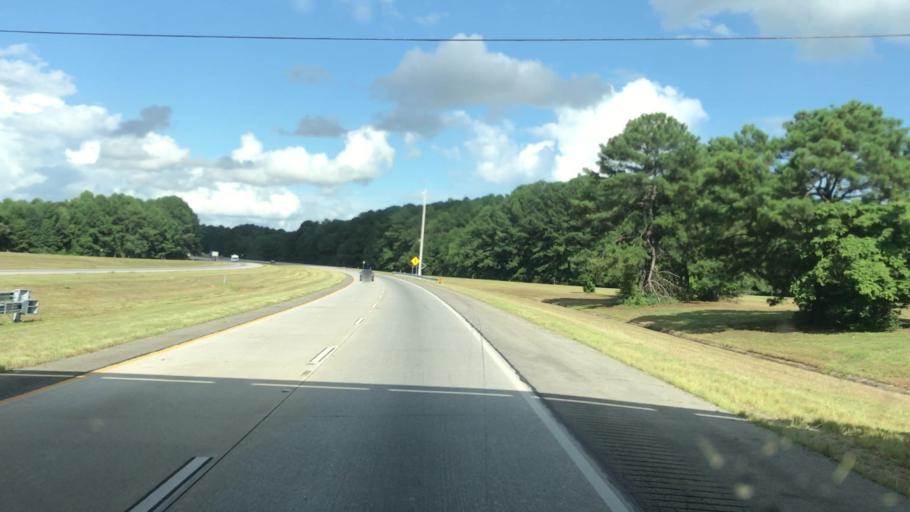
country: US
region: Georgia
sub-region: Greene County
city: Union Point
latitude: 33.5439
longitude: -83.0797
